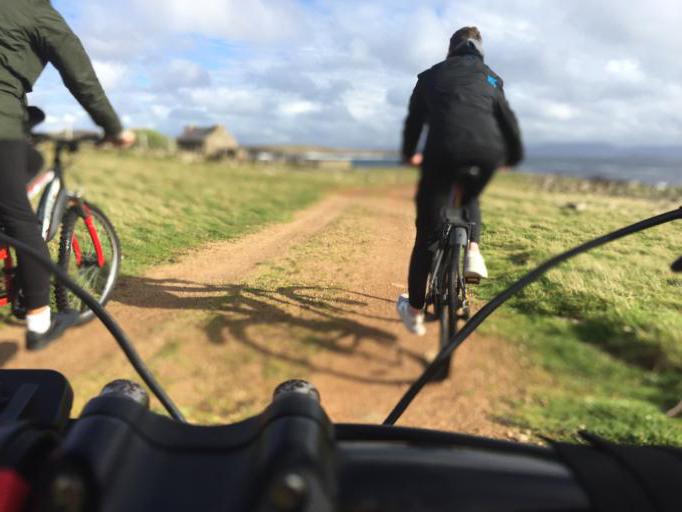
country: IE
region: Ulster
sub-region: County Donegal
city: Derrybeg
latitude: 55.2623
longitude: -8.2329
